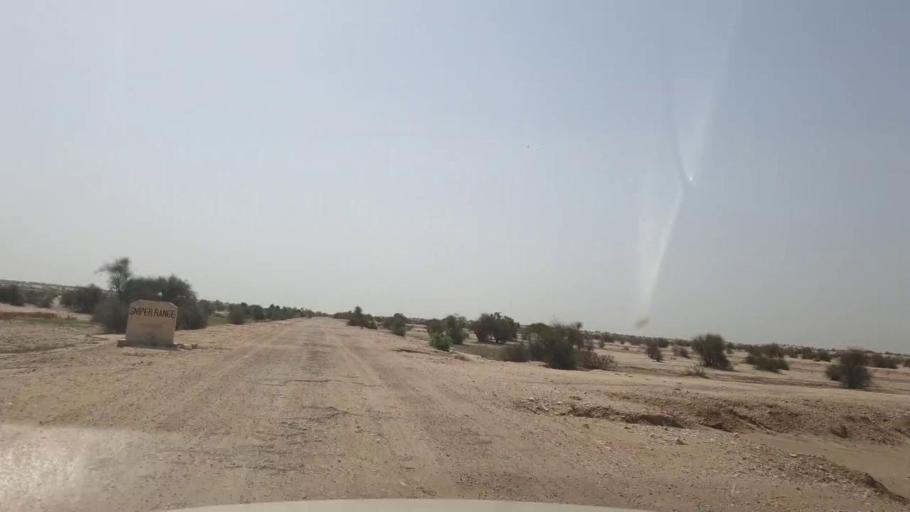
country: PK
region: Sindh
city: Rohri
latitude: 27.4455
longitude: 69.2359
